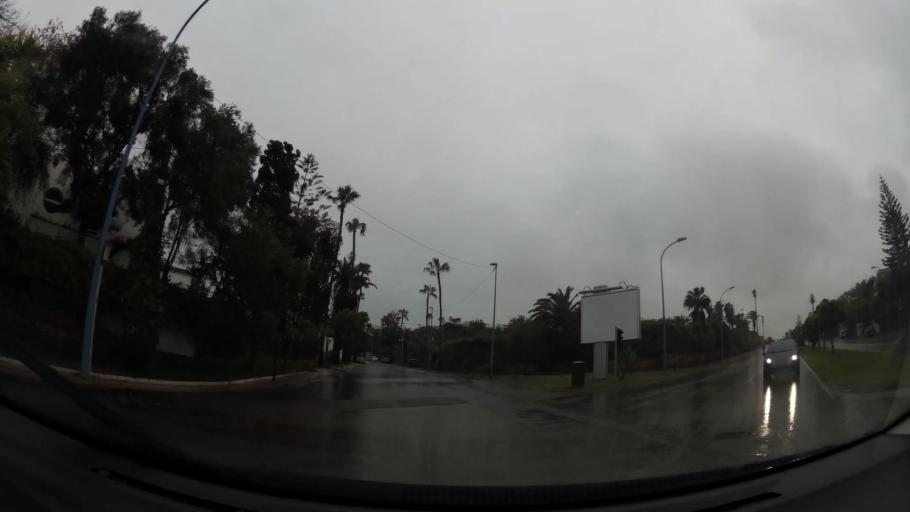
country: MA
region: Grand Casablanca
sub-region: Casablanca
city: Casablanca
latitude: 33.5871
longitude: -7.6727
